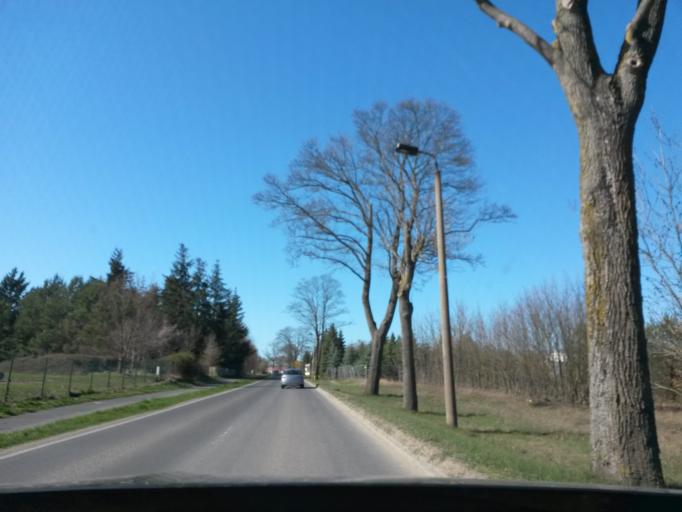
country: DE
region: Brandenburg
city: Rehfelde
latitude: 52.5253
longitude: 13.9281
